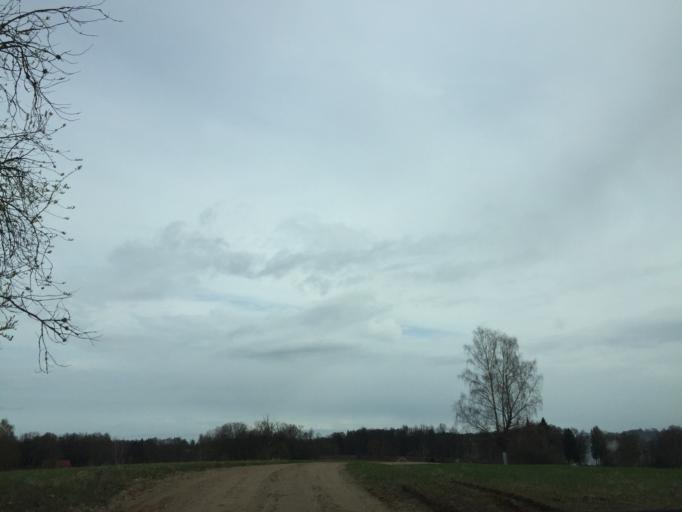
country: LV
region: Amatas Novads
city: Drabesi
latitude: 57.2517
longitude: 25.2745
